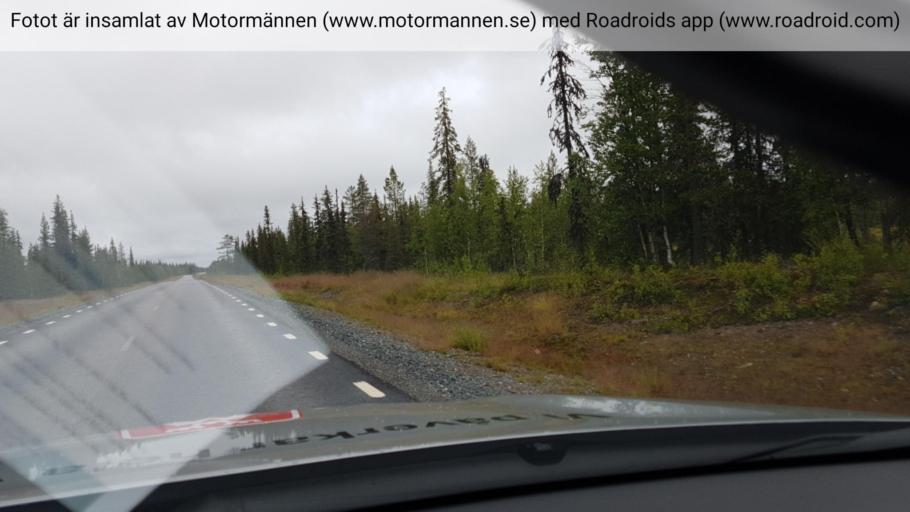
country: SE
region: Norrbotten
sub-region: Gallivare Kommun
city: Gaellivare
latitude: 66.9739
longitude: 20.7454
